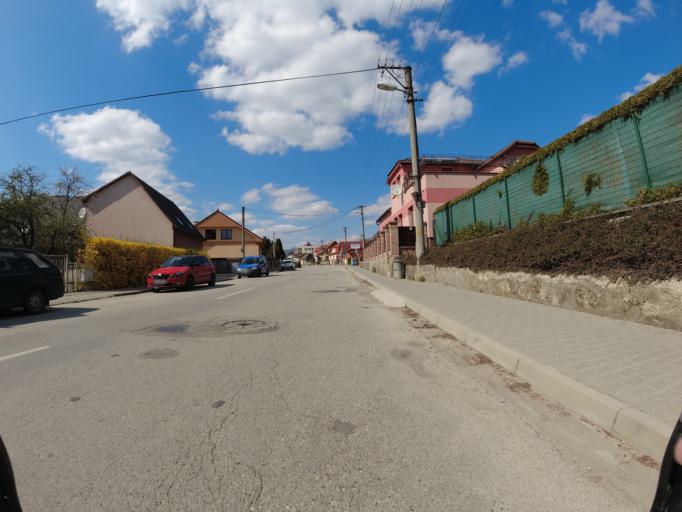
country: SK
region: Nitriansky
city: Stara Tura
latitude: 48.7758
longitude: 17.6983
